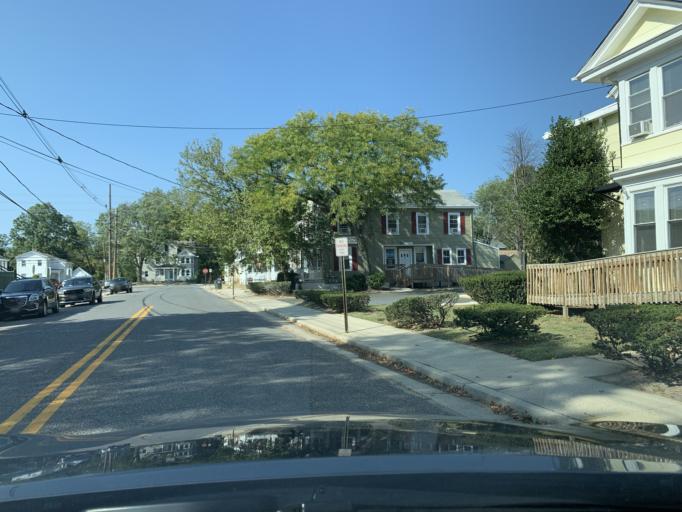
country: US
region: New Jersey
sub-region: Monmouth County
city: Eatontown
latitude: 40.3058
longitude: -74.0577
